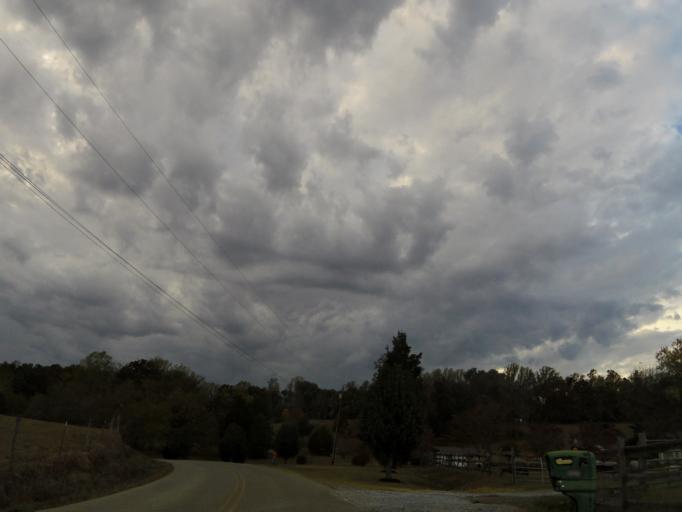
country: US
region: Tennessee
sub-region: Blount County
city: Louisville
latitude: 35.7856
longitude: -84.0594
